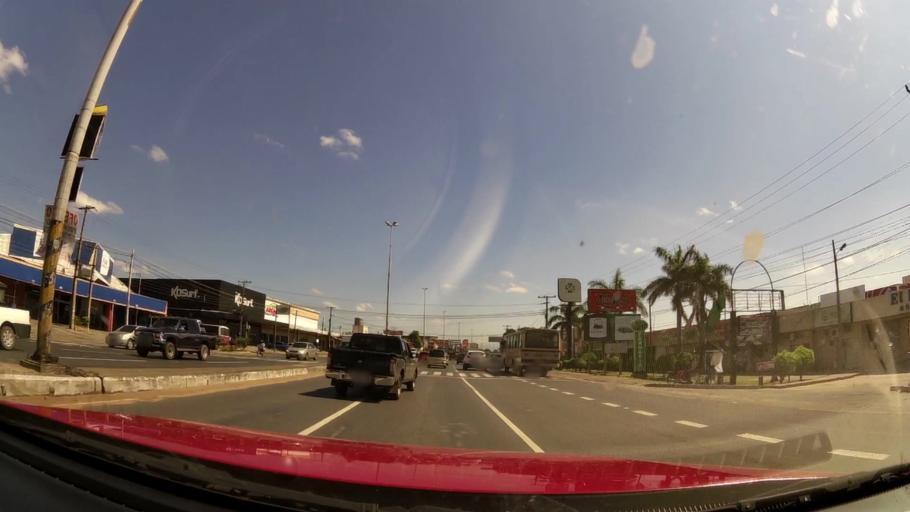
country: PY
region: Central
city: Colonia Mariano Roque Alonso
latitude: -25.2383
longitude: -57.5410
